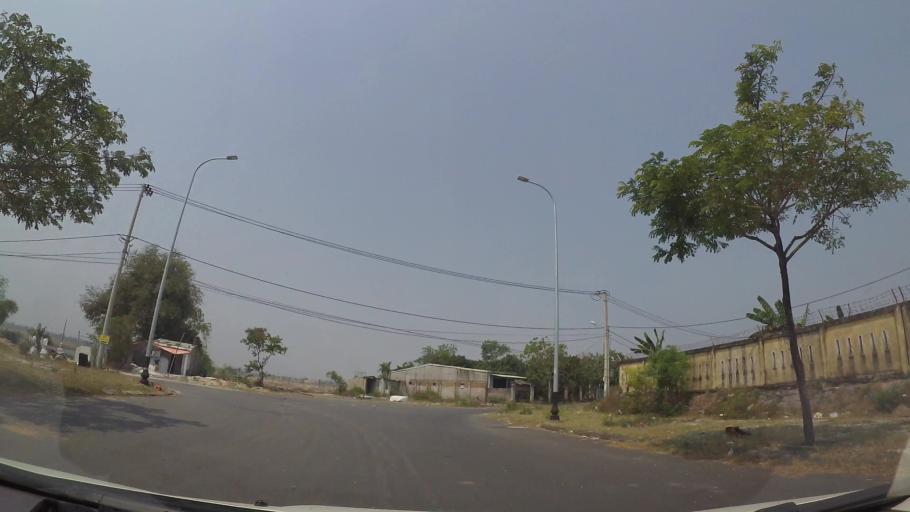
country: VN
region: Da Nang
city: Ngu Hanh Son
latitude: 16.0066
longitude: 108.2535
